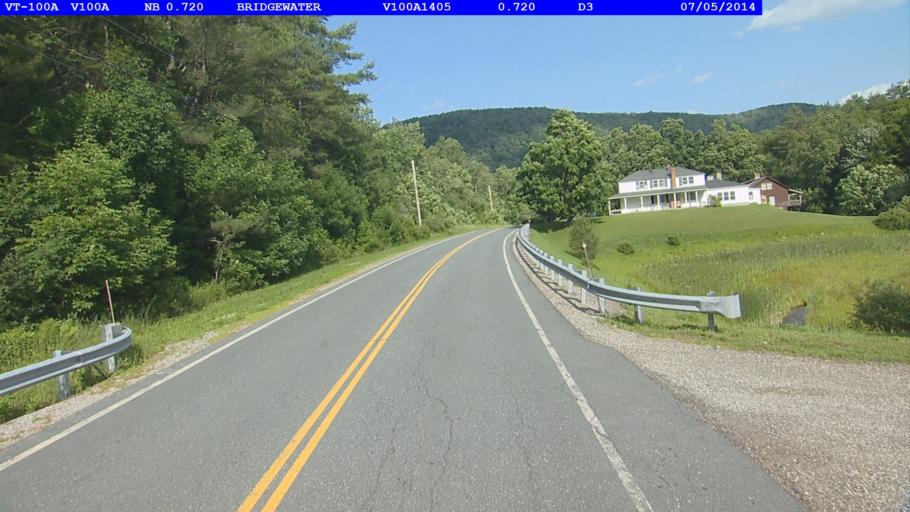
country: US
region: Vermont
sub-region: Windsor County
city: Woodstock
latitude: 43.5337
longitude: -72.7267
